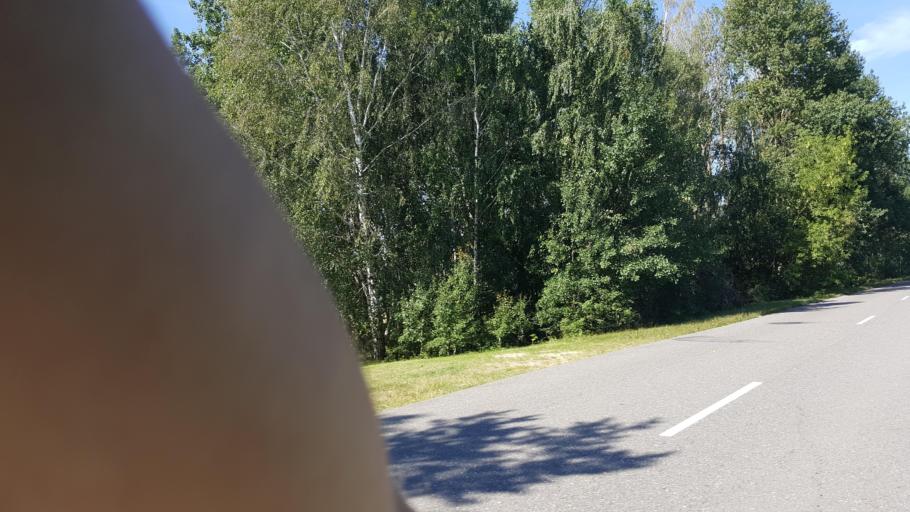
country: BY
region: Brest
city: Charnawchytsy
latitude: 52.2892
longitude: 23.7785
